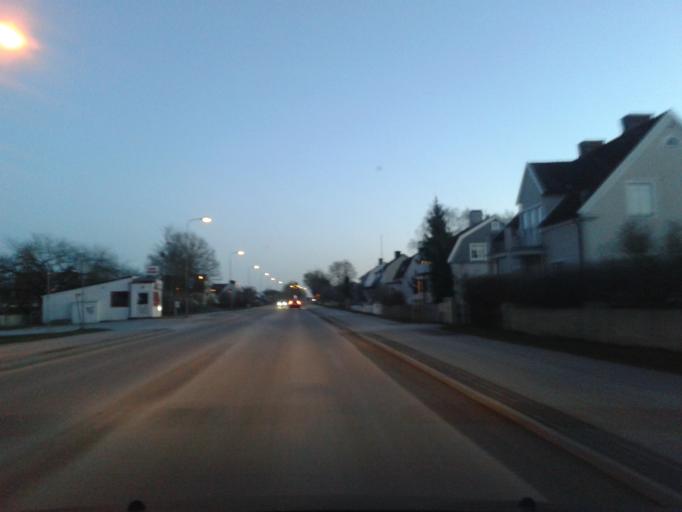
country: SE
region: Gotland
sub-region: Gotland
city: Visby
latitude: 57.6321
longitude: 18.3119
